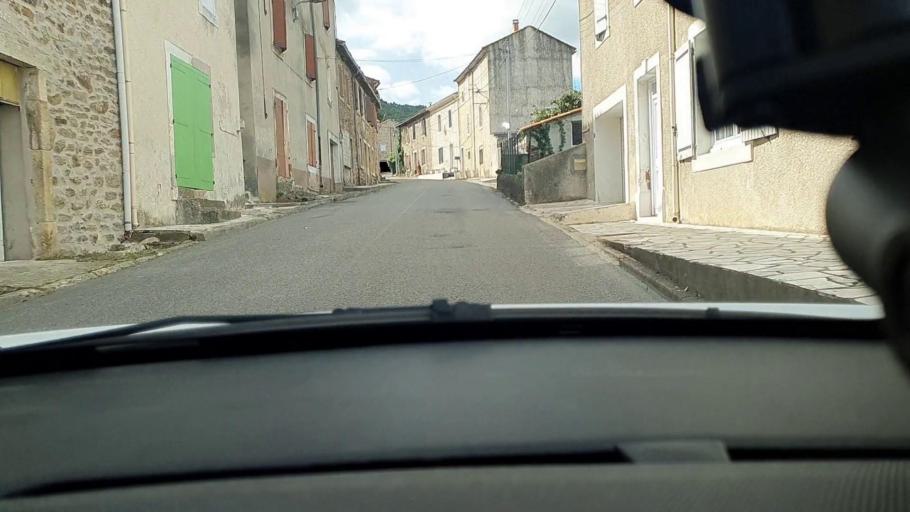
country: FR
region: Languedoc-Roussillon
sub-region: Departement du Gard
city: Branoux-les-Taillades
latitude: 44.2872
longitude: 4.0068
